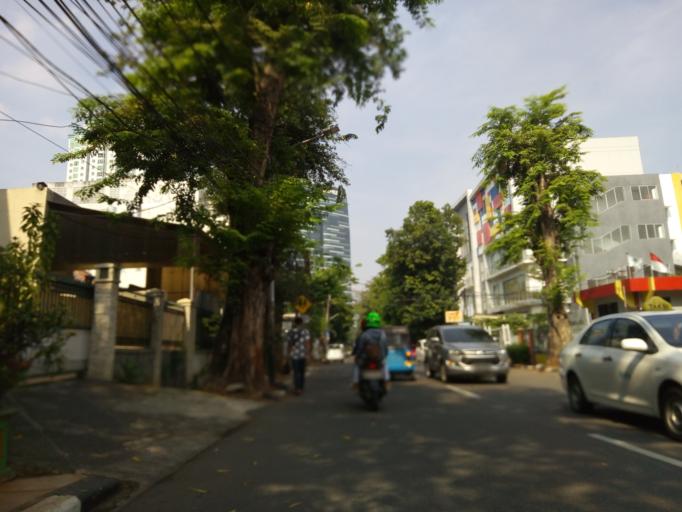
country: ID
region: Jakarta Raya
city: Jakarta
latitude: -6.2071
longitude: 106.8337
